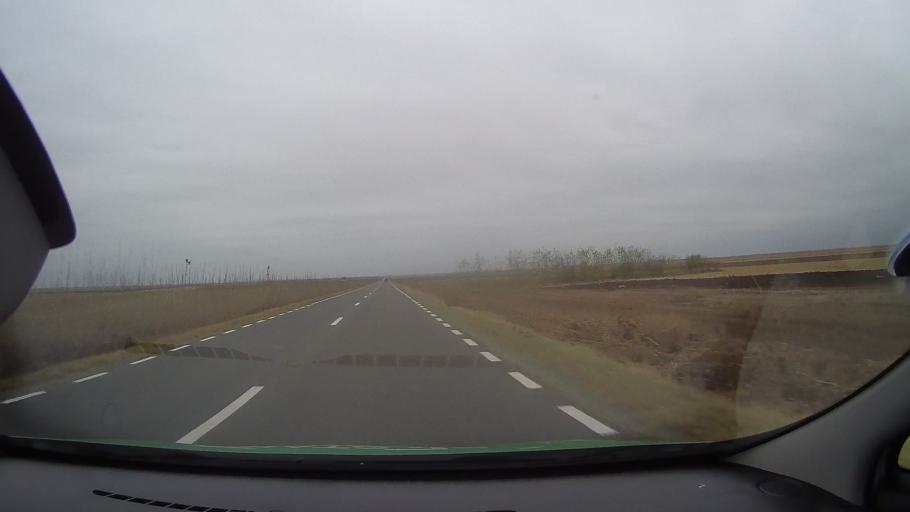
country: RO
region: Ialomita
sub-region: Comuna Gheorghe Lazar
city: Gheorghe Lazar
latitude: 44.6471
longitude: 27.4054
